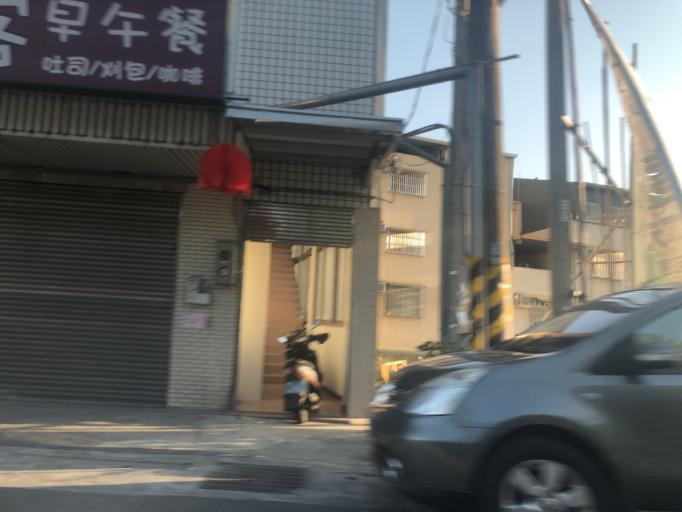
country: TW
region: Taiwan
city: Fengyuan
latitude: 24.2757
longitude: 120.7788
